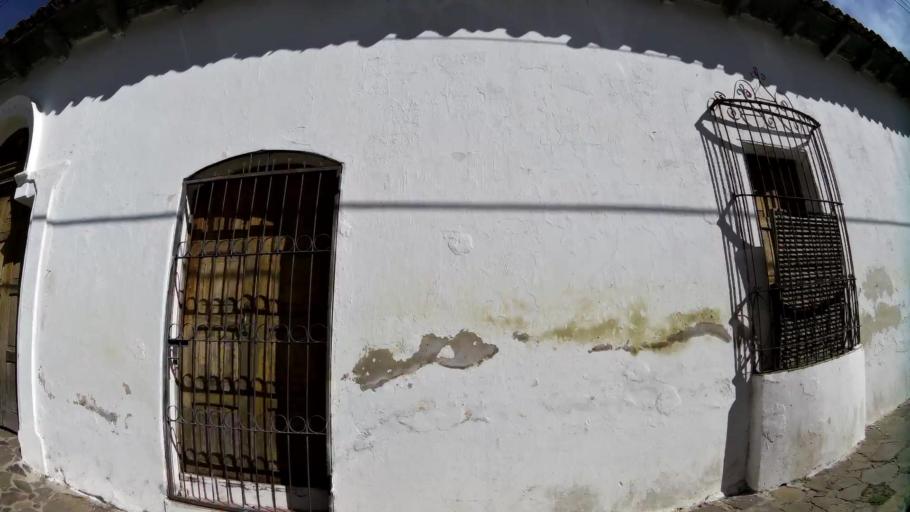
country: SV
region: Cuscatlan
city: Suchitoto
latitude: 13.9377
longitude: -89.0266
